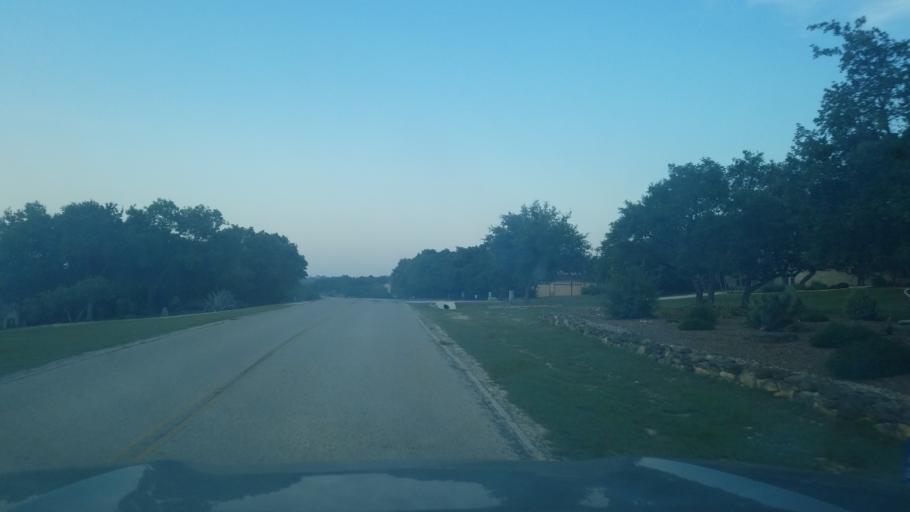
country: US
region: Texas
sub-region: Comal County
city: Bulverde
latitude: 29.8268
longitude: -98.4027
